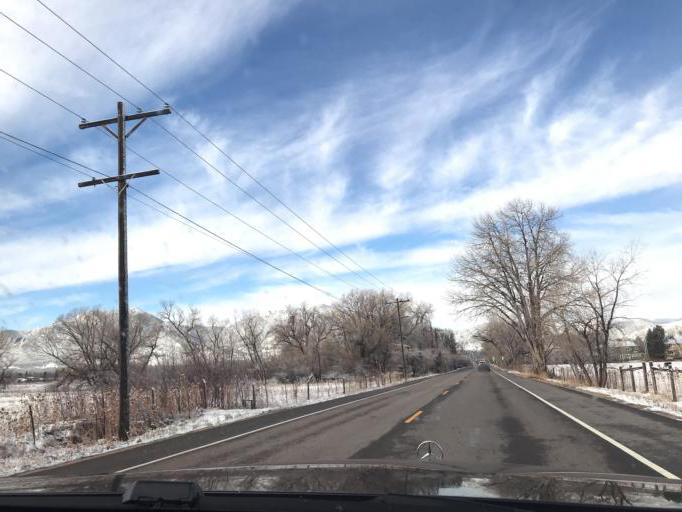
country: US
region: Colorado
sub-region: Boulder County
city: Boulder
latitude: 40.0001
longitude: -105.2172
